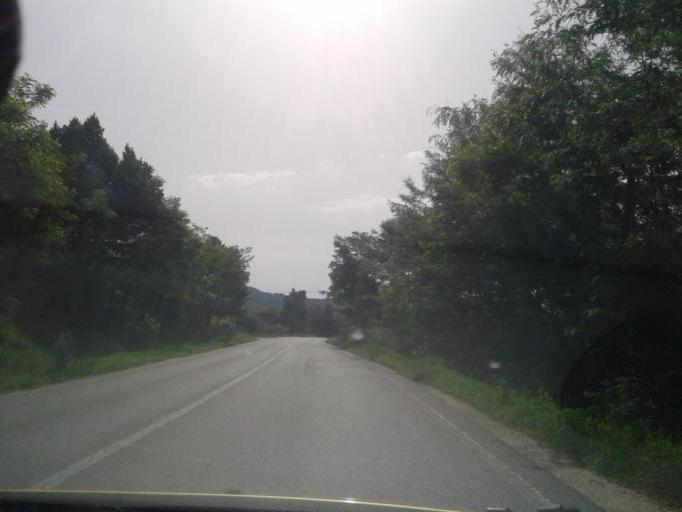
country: RO
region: Valcea
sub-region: Comuna Bunesti
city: Bunesti
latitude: 45.1106
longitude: 24.1821
